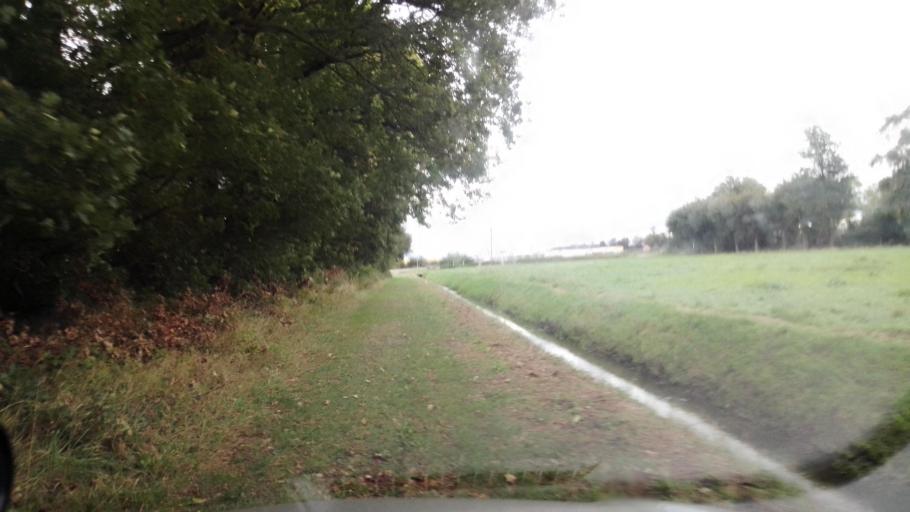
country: NL
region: Limburg
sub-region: Gemeente Peel en Maas
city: Maasbree
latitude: 51.4250
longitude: 6.0983
